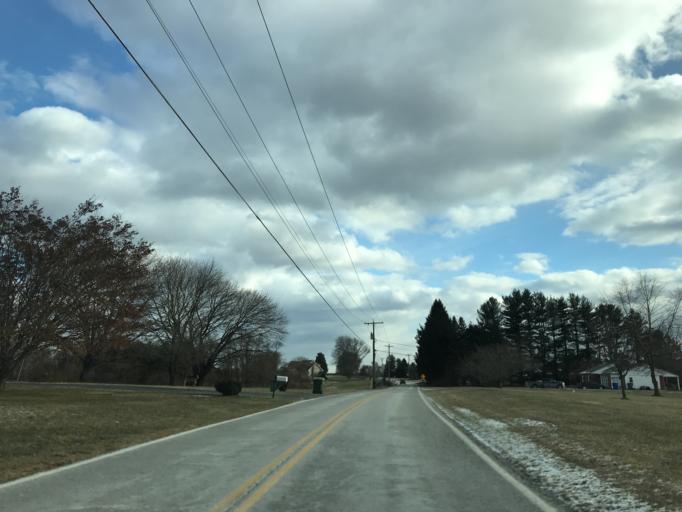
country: US
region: Maryland
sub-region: Harford County
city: Jarrettsville
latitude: 39.6139
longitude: -76.4472
